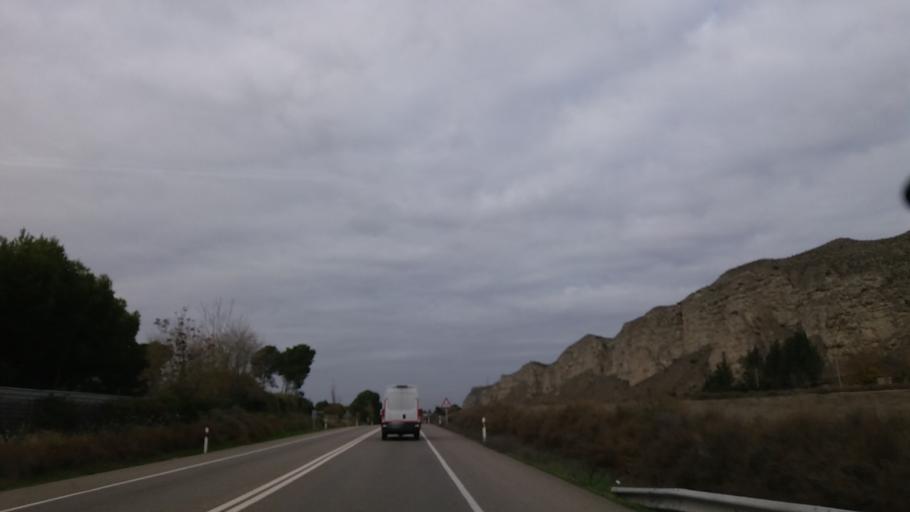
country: ES
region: Aragon
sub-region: Provincia de Zaragoza
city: Nuez de Ebro
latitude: 41.5872
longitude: -0.6624
